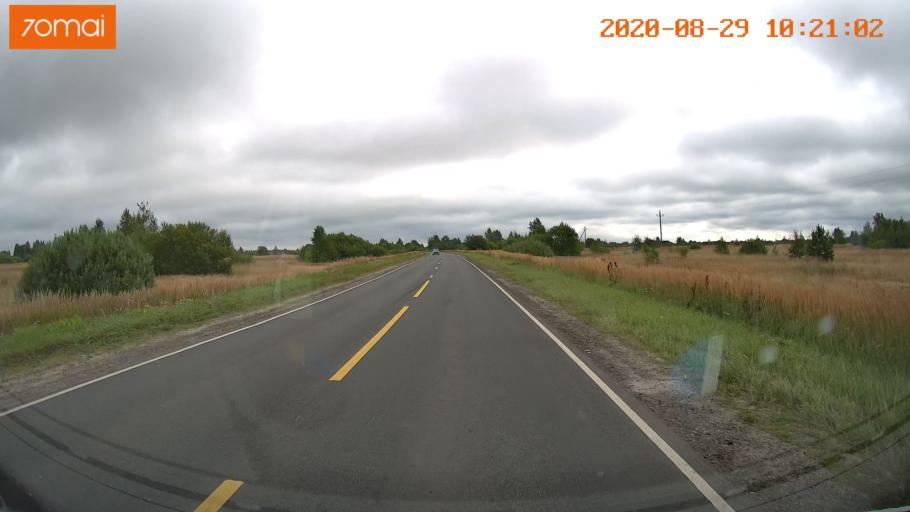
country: RU
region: Ivanovo
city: Yur'yevets
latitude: 57.3229
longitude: 42.9078
